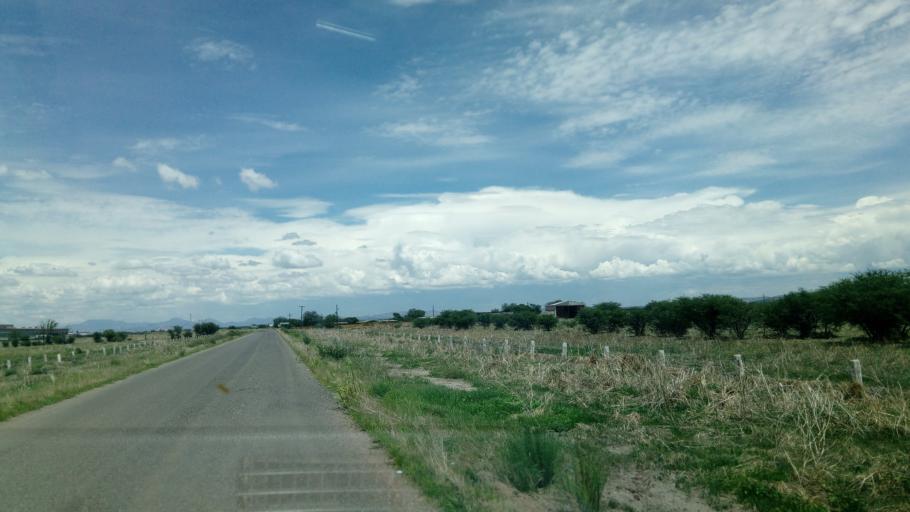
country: MX
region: Durango
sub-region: Durango
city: Jose Refugio Salcido
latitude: 24.1659
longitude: -104.5007
